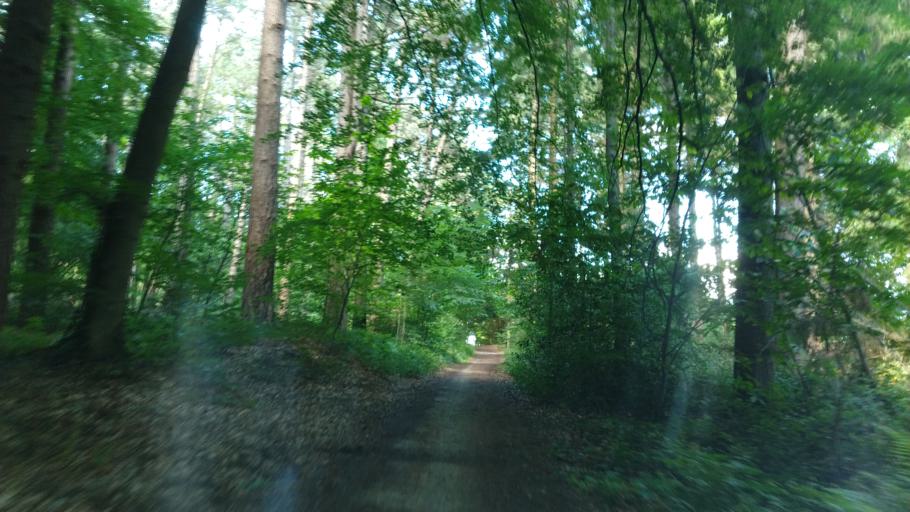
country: BE
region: Flanders
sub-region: Provincie Vlaams-Brabant
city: Bierbeek
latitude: 50.8148
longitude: 4.7477
